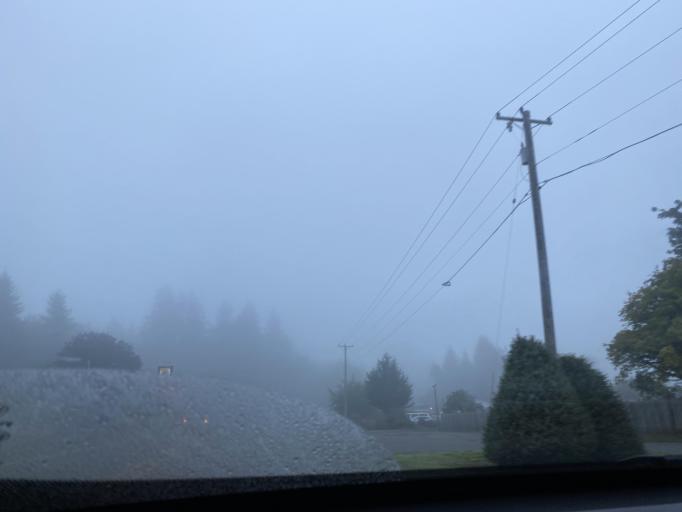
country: US
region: Washington
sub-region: Clallam County
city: Forks
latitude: 47.9405
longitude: -124.3860
